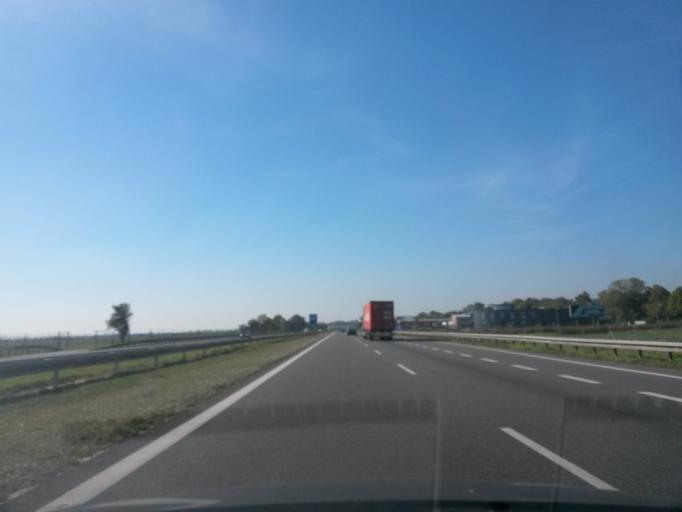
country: PL
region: Lesser Poland Voivodeship
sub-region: Powiat krakowski
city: Balice
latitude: 50.0815
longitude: 19.7792
